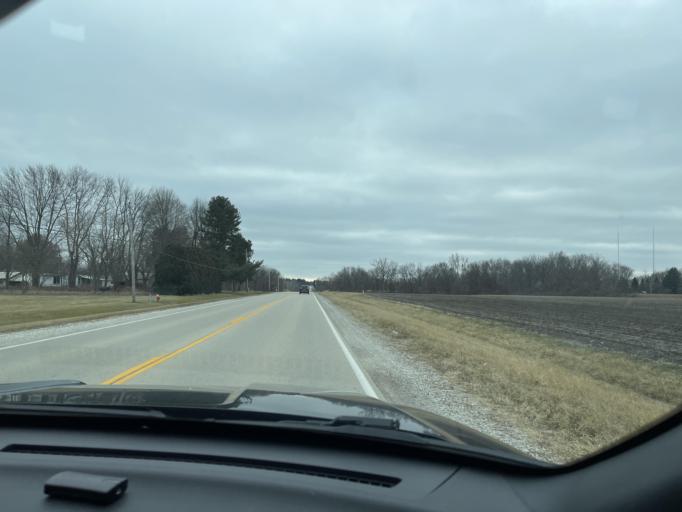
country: US
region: Illinois
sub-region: Sangamon County
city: Leland Grove
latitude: 39.8176
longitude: -89.7397
